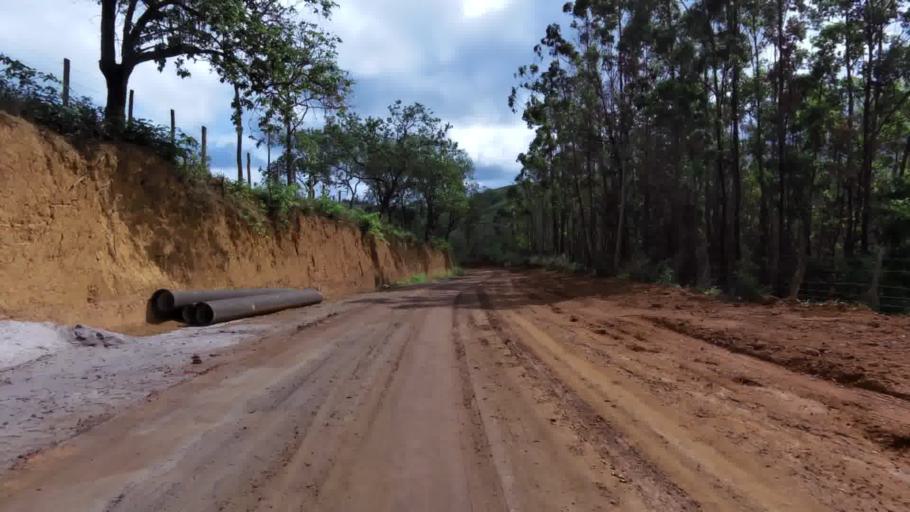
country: BR
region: Espirito Santo
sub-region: Piuma
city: Piuma
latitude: -20.8117
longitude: -40.6691
